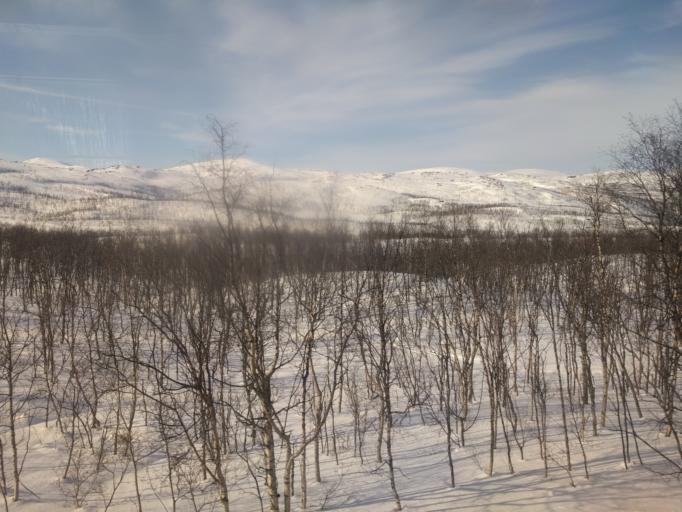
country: NO
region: Troms
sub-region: Bardu
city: Setermoen
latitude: 68.4260
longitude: 18.4554
